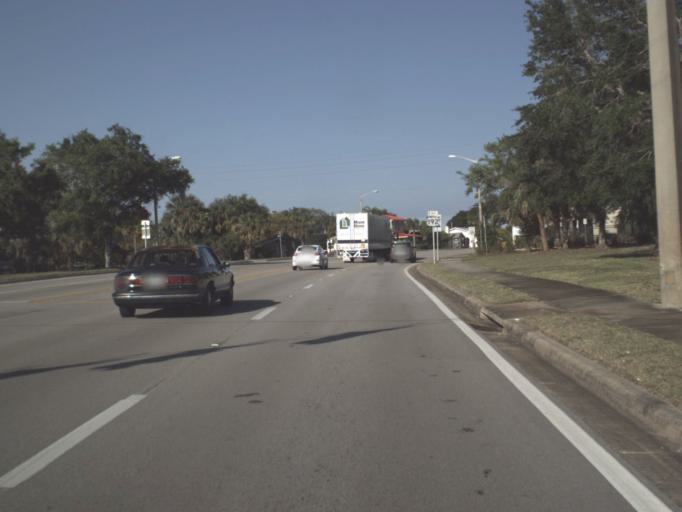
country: US
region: Florida
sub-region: Brevard County
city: Melbourne
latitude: 28.0790
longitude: -80.6161
